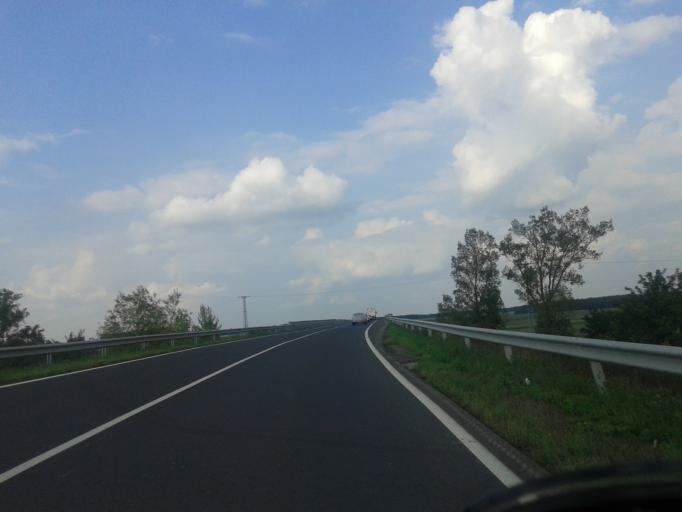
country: HU
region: Bacs-Kiskun
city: Apostag
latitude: 46.8732
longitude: 18.9784
